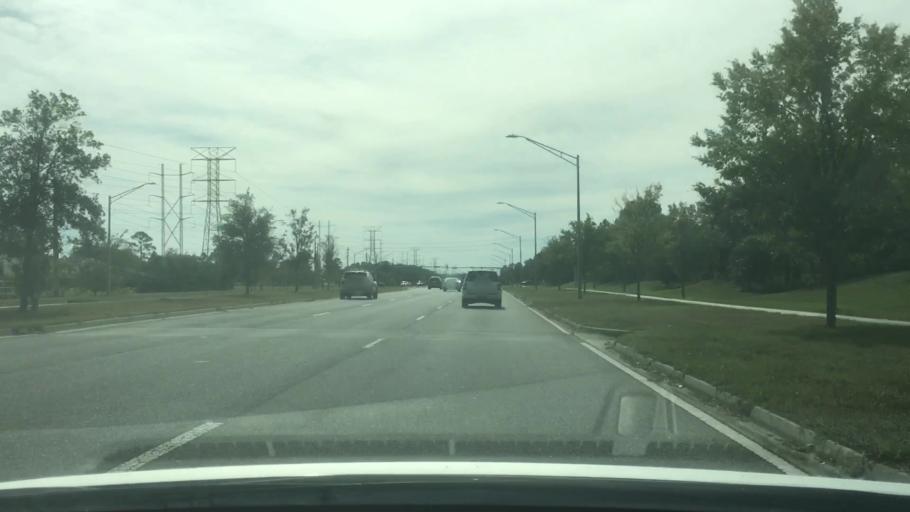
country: US
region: Florida
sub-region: Duval County
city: Atlantic Beach
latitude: 30.3146
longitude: -81.4894
